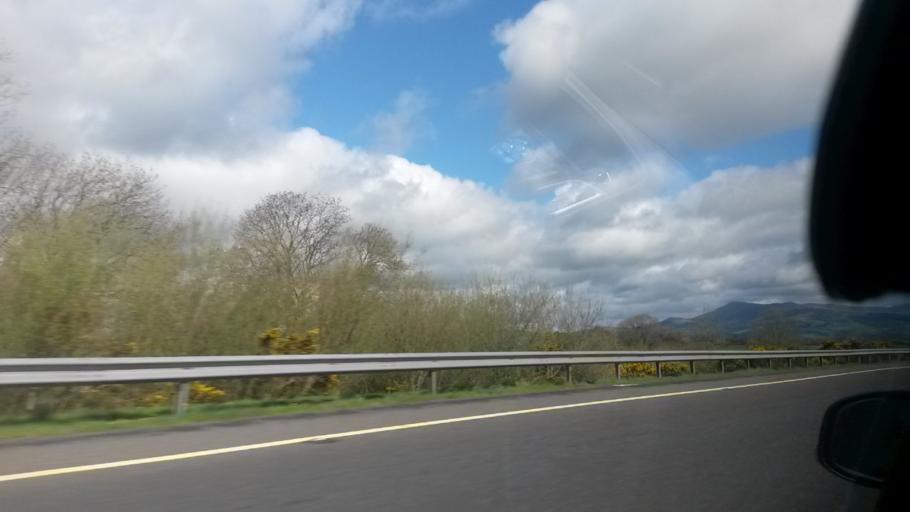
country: IE
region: Munster
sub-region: County Cork
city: Mitchelstown
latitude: 52.2352
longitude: -8.2841
